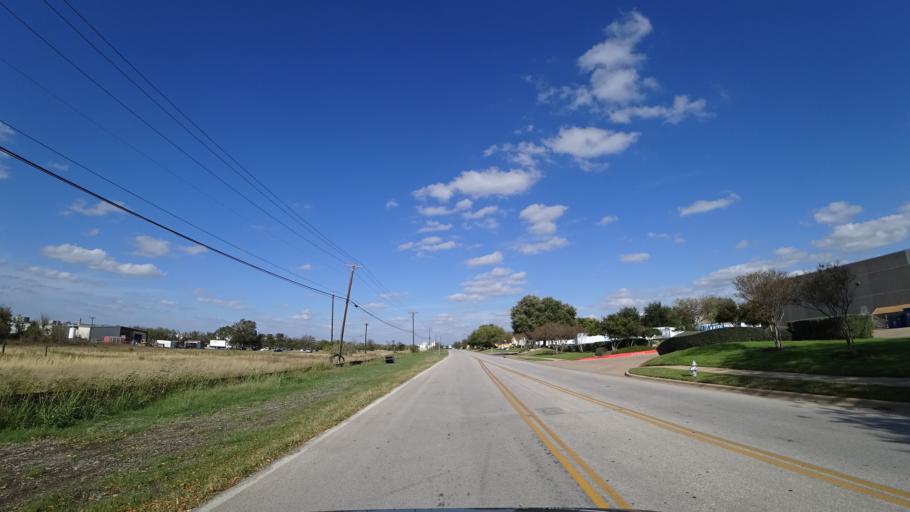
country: US
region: Texas
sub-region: Travis County
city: Wells Branch
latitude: 30.4591
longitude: -97.6767
